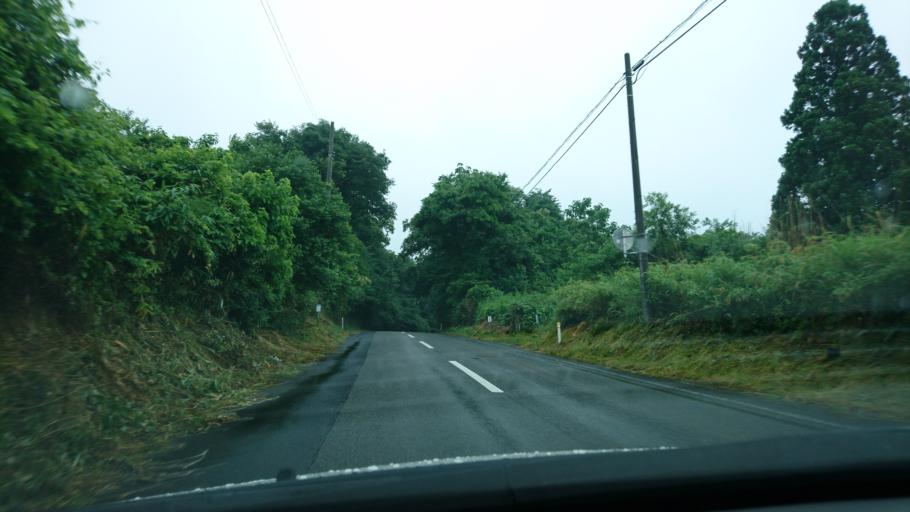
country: JP
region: Iwate
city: Ichinoseki
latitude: 38.9086
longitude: 141.0320
